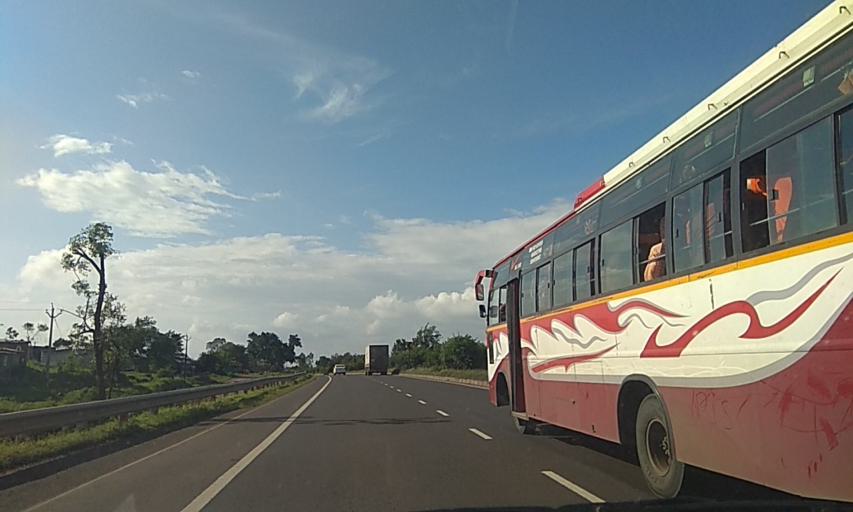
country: IN
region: Maharashtra
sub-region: Satara Division
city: Karad
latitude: 17.3305
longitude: 74.1456
